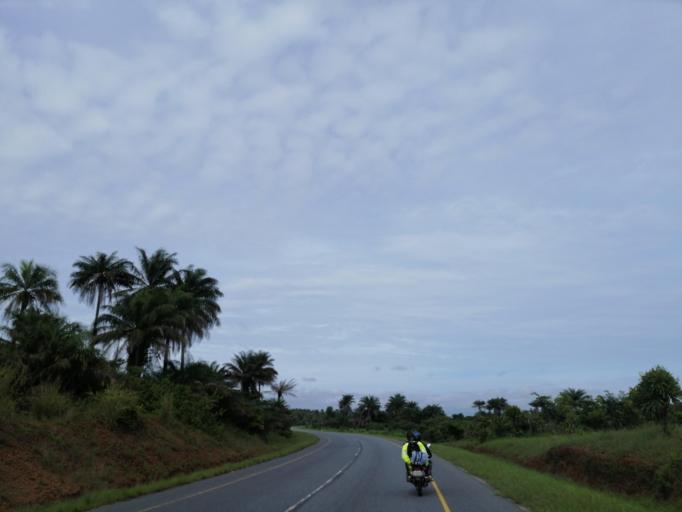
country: SL
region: Northern Province
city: Port Loko
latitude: 8.7696
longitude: -12.8831
